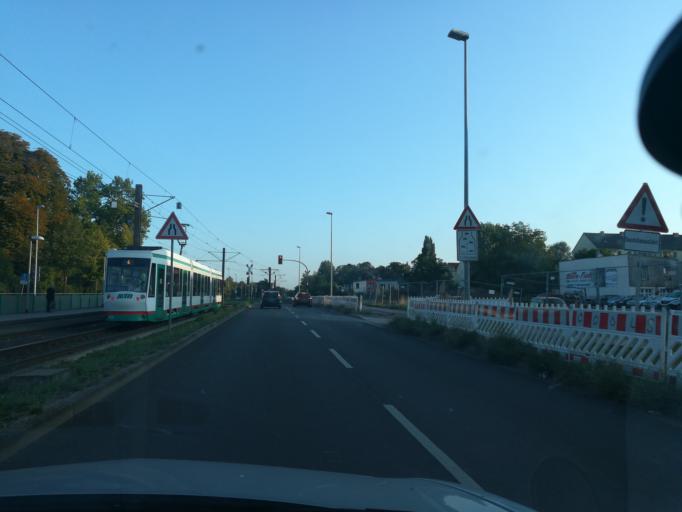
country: DE
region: Saxony-Anhalt
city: Magdeburg
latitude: 52.1302
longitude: 11.6052
